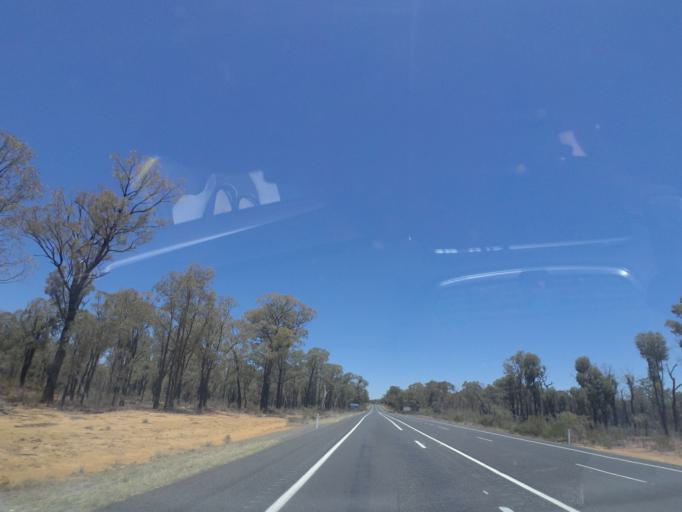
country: AU
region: New South Wales
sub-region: Warrumbungle Shire
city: Coonabarabran
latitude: -30.8793
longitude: 149.4470
